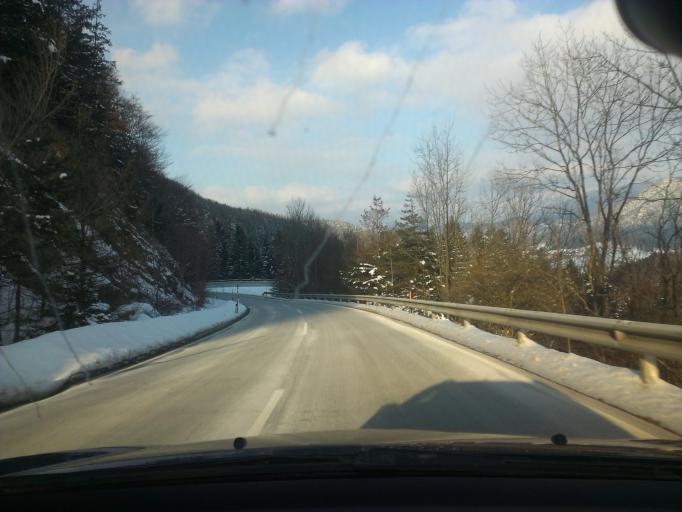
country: AT
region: Lower Austria
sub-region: Politischer Bezirk Wiener Neustadt
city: Miesenbach
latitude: 47.8206
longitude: 15.9530
